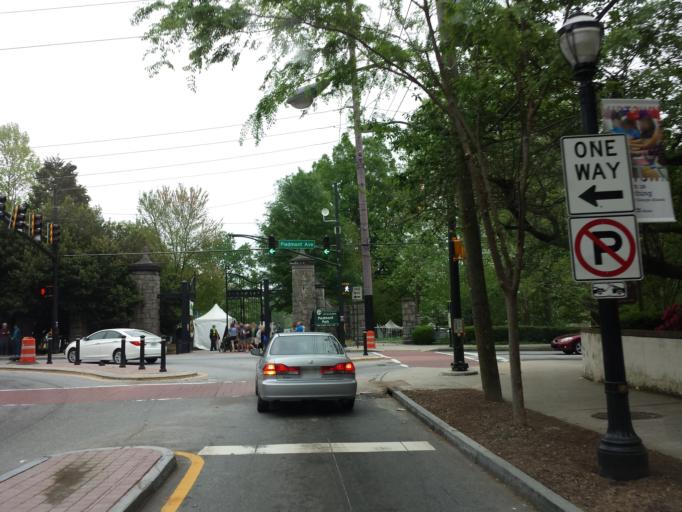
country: US
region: Georgia
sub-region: Fulton County
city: Atlanta
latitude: 33.7864
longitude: -84.3784
